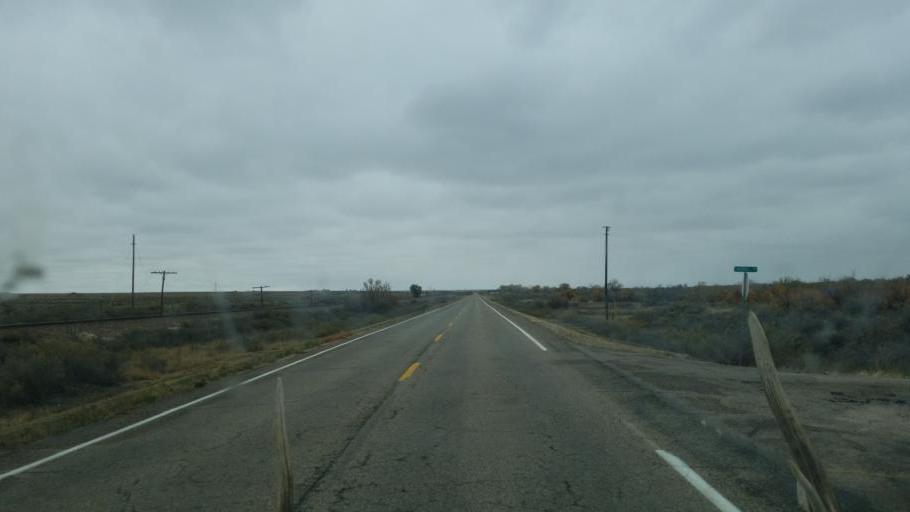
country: US
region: Colorado
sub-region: Otero County
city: Fowler
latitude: 38.2538
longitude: -104.2995
